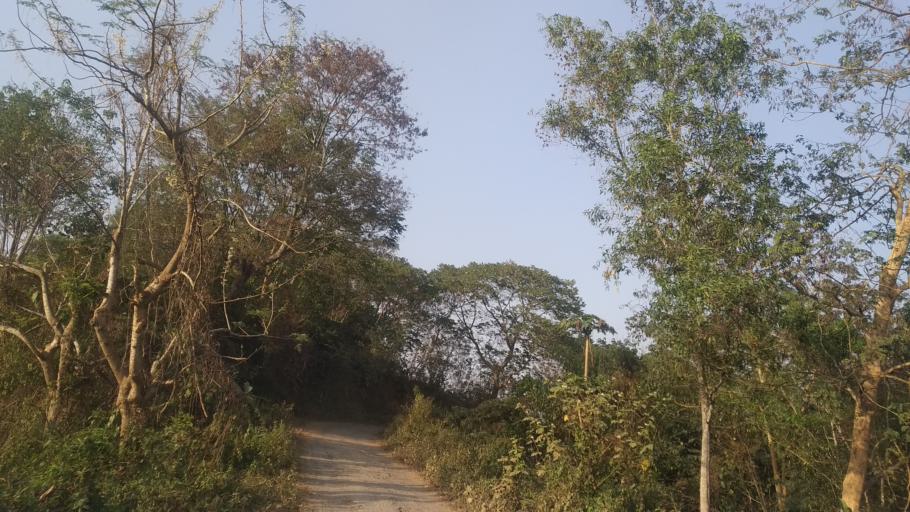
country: IN
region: Tripura
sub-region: West Tripura
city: Sonamura
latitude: 23.4368
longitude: 91.3593
